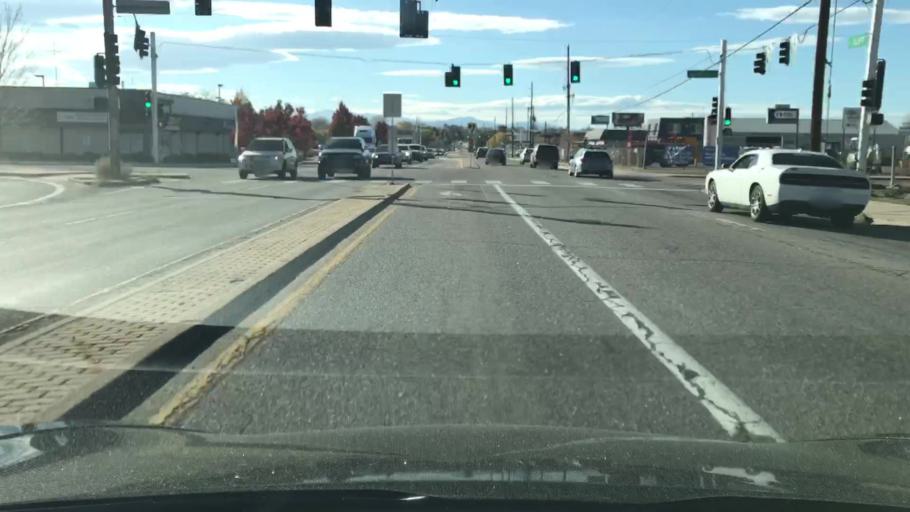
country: US
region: Colorado
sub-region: Arapahoe County
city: Glendale
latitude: 39.6748
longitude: -104.8889
